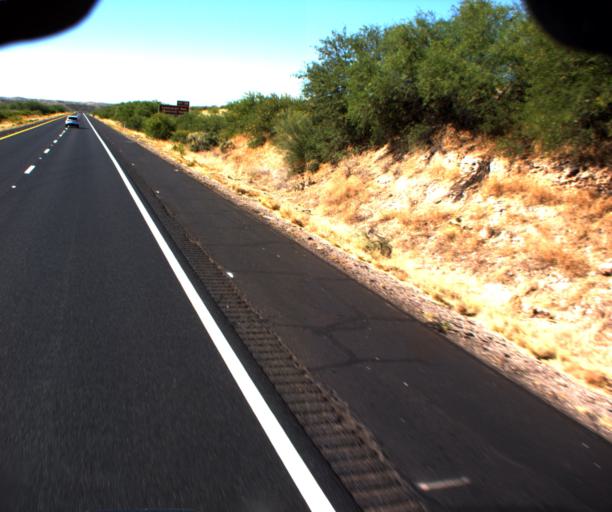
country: US
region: Arizona
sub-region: Santa Cruz County
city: Tubac
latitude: 31.5659
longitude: -111.0536
